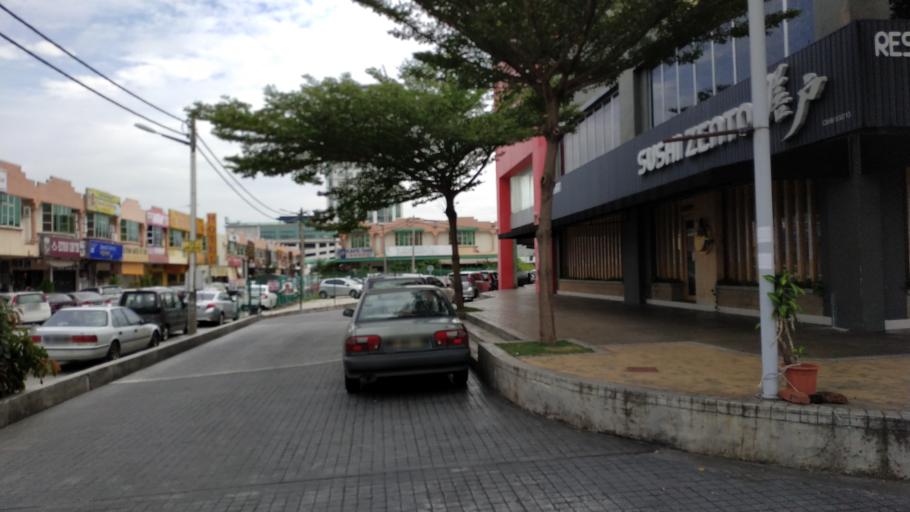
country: MY
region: Perak
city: Ipoh
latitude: 4.6191
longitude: 101.1175
